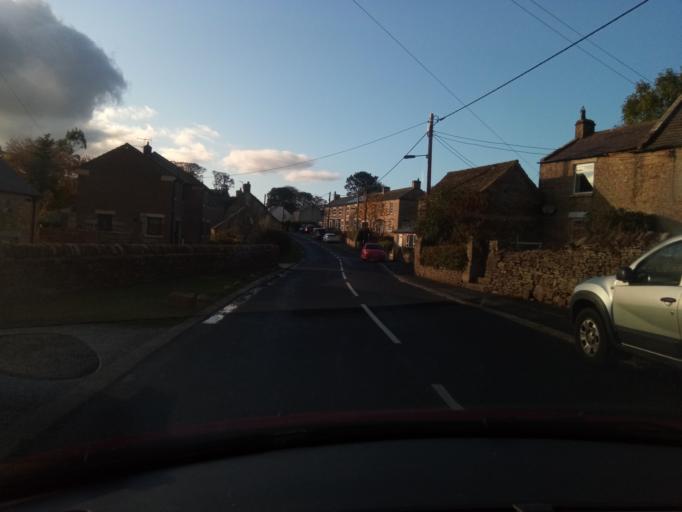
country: GB
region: England
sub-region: County Durham
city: Hamsterley
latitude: 54.6745
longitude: -1.8177
